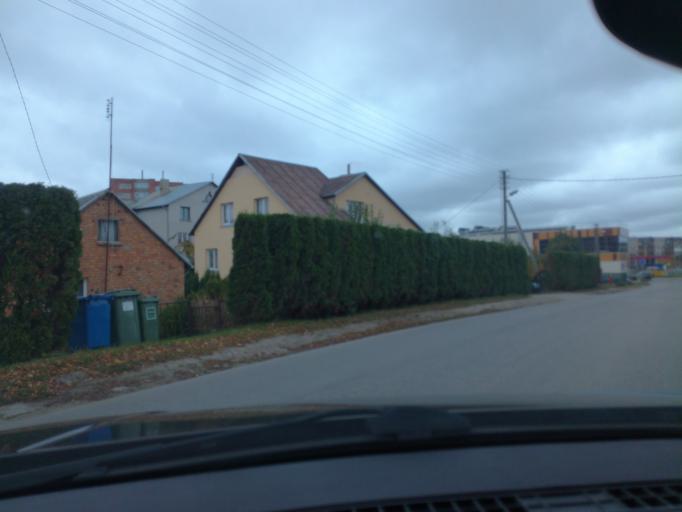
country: LT
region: Alytaus apskritis
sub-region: Alytus
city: Alytus
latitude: 54.4085
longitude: 24.0143
